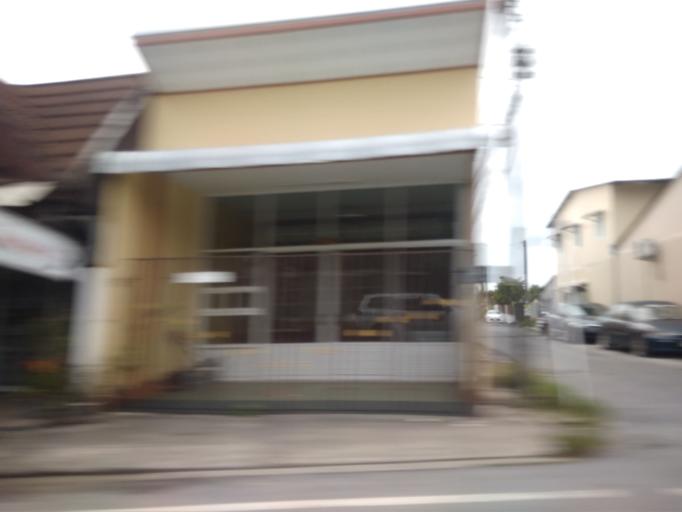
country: TH
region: Phuket
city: Mueang Phuket
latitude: 7.8666
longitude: 98.3806
